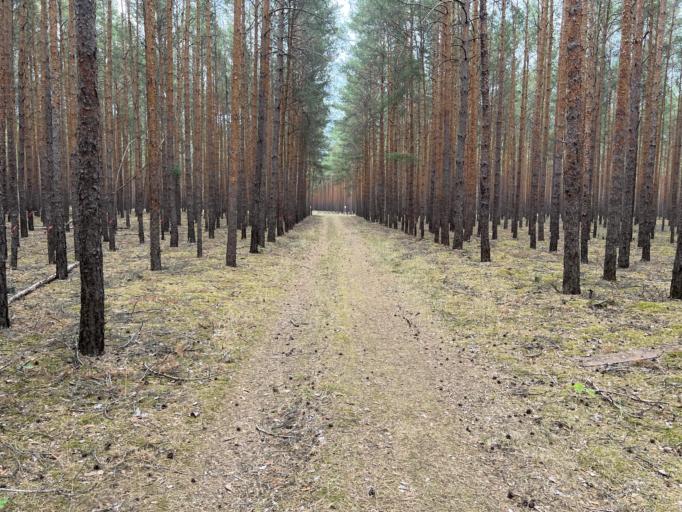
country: DE
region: Brandenburg
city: Gross Koris
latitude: 52.2193
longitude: 13.7393
